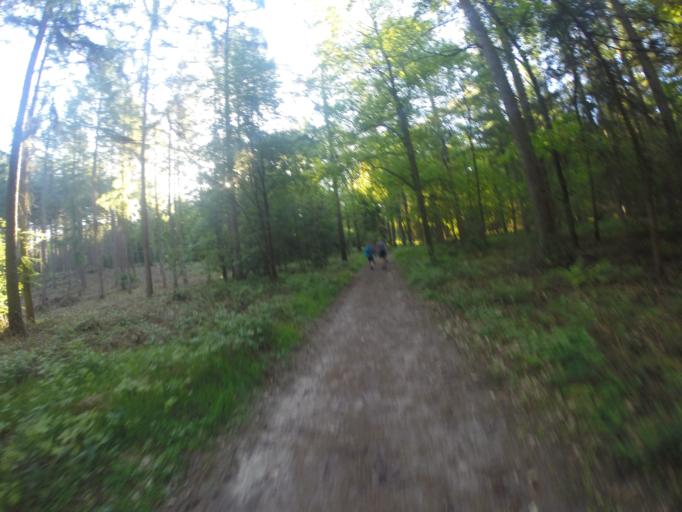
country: NL
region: Gelderland
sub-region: Gemeente Montferland
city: s-Heerenberg
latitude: 51.9075
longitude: 6.2049
